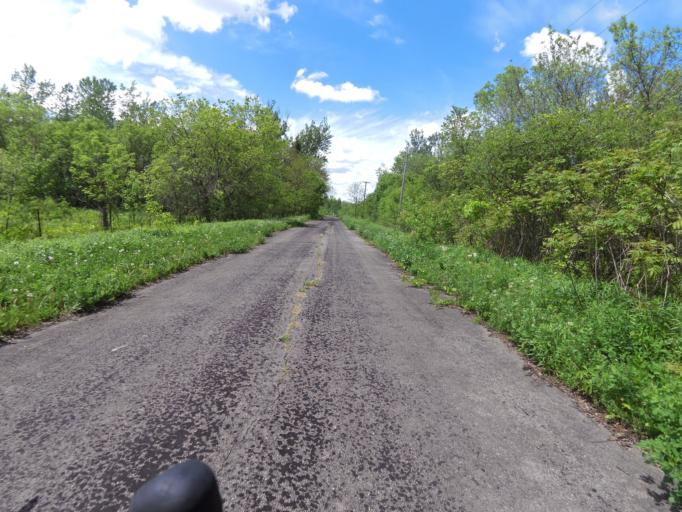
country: CA
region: Ontario
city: Ottawa
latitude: 45.4087
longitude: -75.5361
